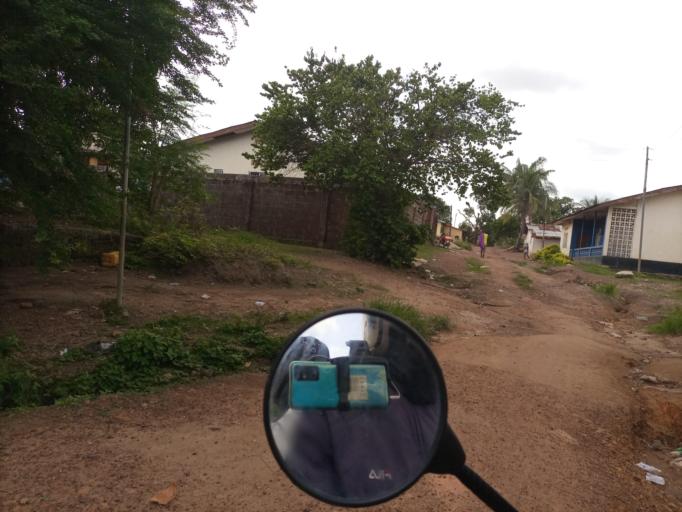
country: SL
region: Southern Province
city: Bo
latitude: 7.9481
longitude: -11.7332
